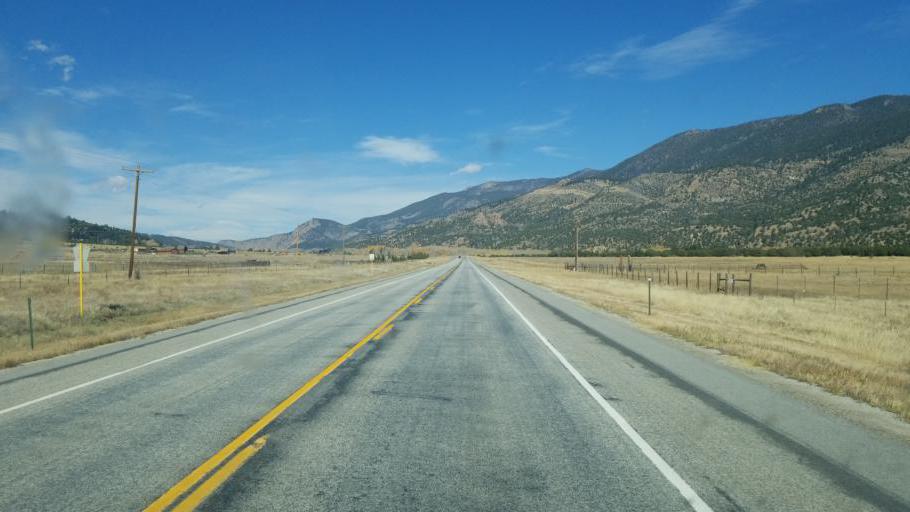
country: US
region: Colorado
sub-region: Chaffee County
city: Buena Vista
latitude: 38.9244
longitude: -106.1824
